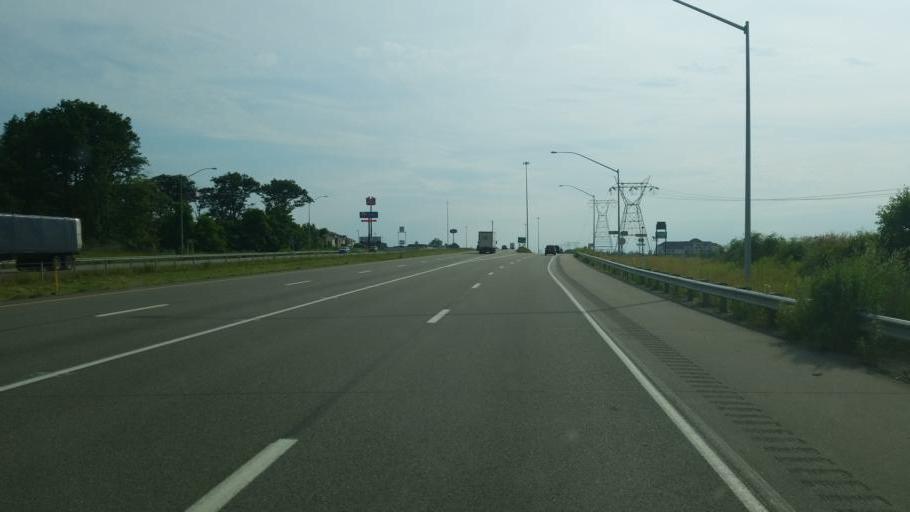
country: US
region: Pennsylvania
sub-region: Erie County
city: Erie
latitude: 42.0516
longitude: -80.0759
